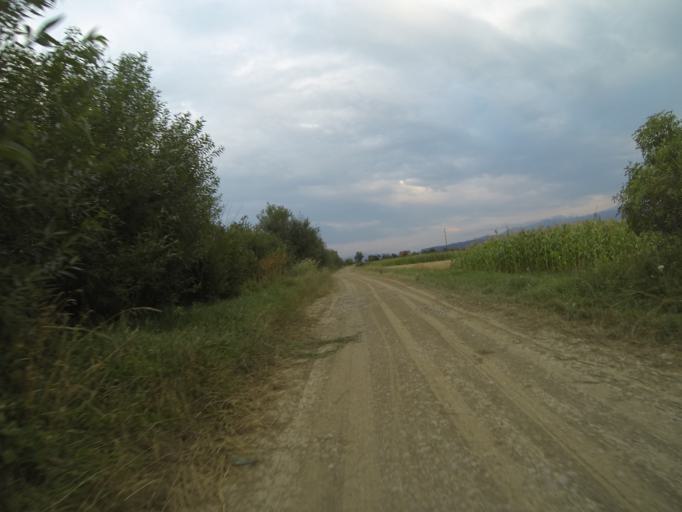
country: RO
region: Brasov
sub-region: Comuna Sinca Veche
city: Sinca Veche
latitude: 45.7724
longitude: 25.1702
